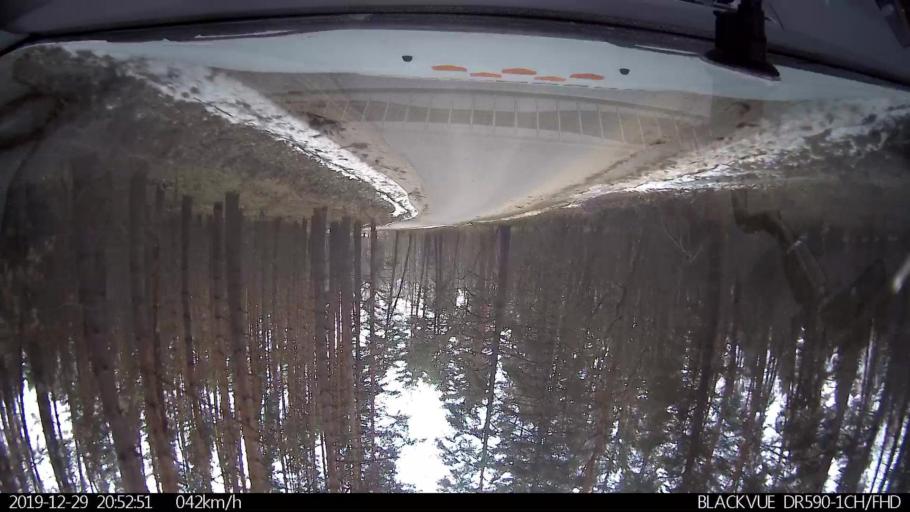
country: RU
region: Nizjnij Novgorod
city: Afonino
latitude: 56.1750
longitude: 43.9909
